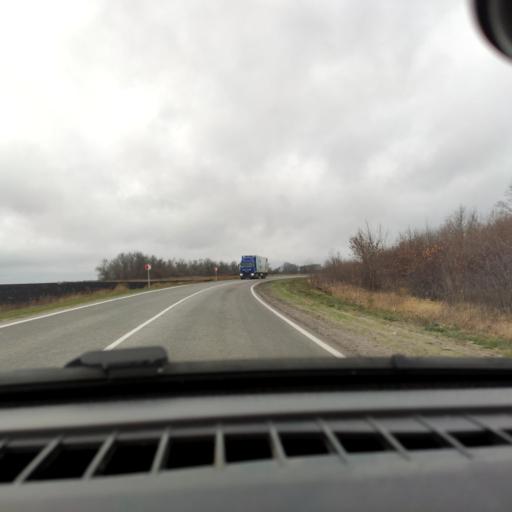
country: RU
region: Voronezj
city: Shilovo
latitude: 51.3882
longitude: 39.0036
